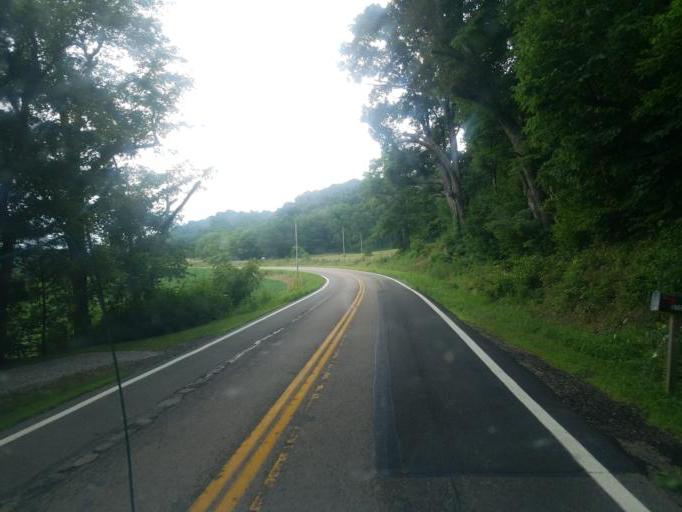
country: US
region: Ohio
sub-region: Knox County
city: Oak Hill
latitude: 40.3449
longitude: -82.0670
